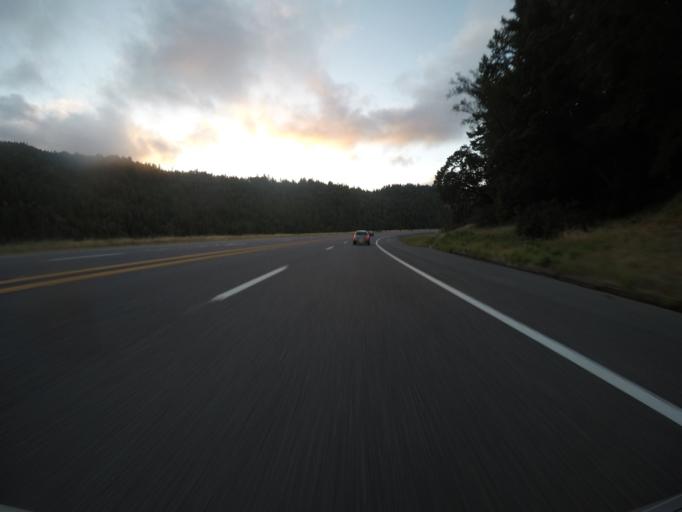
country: US
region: California
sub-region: Humboldt County
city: Redway
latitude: 40.0503
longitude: -123.7919
